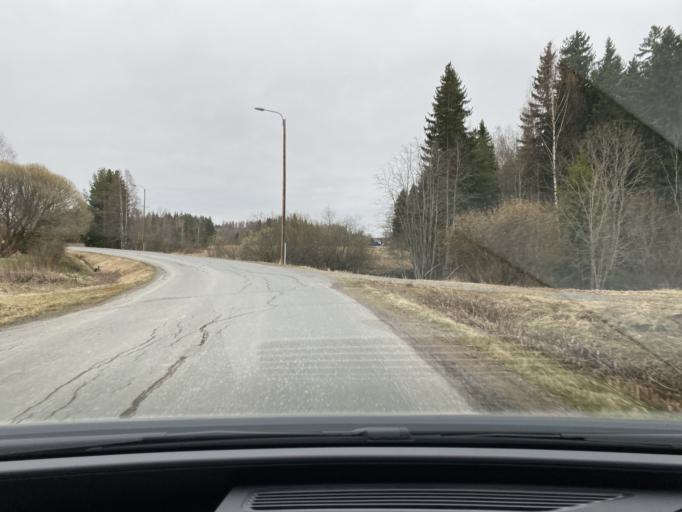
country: FI
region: Satakunta
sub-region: Pori
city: Huittinen
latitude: 61.1643
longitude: 22.7258
